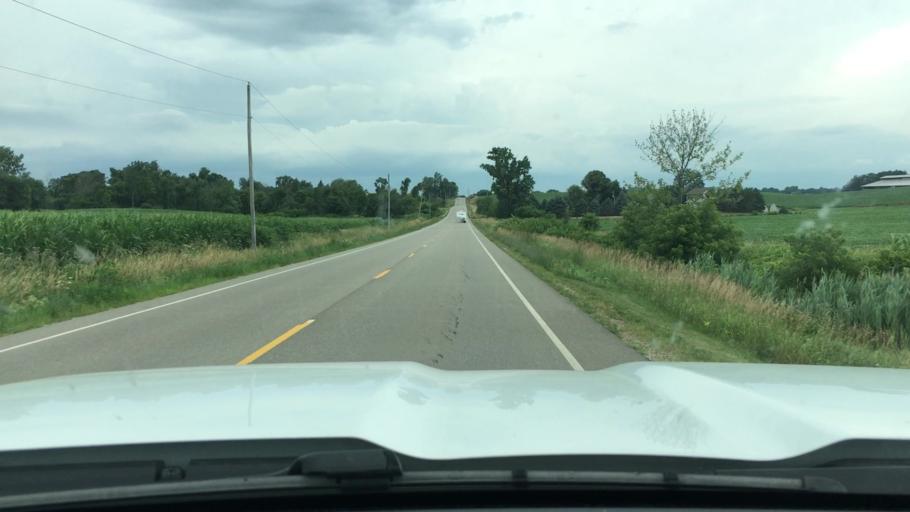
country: US
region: Michigan
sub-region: Ottawa County
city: Hudsonville
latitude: 42.7823
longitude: -85.8229
